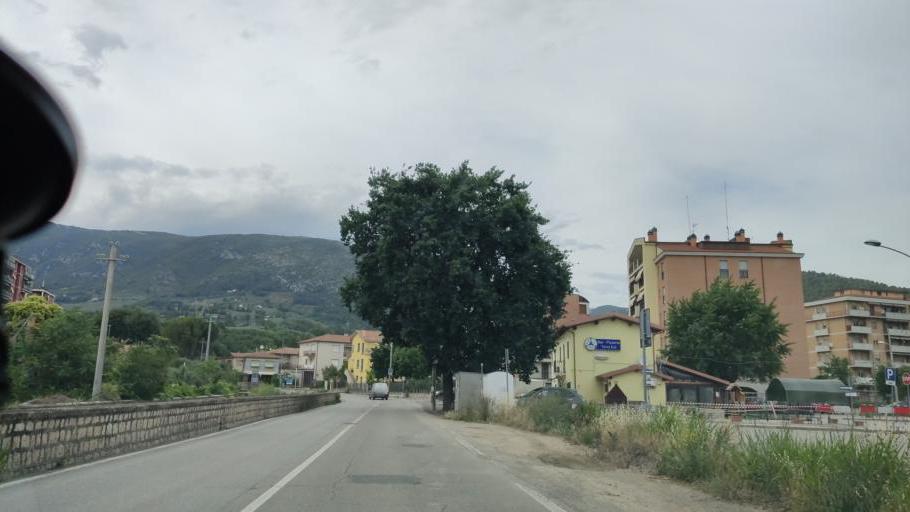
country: IT
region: Umbria
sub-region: Provincia di Terni
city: Terni
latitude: 42.5758
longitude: 12.6750
